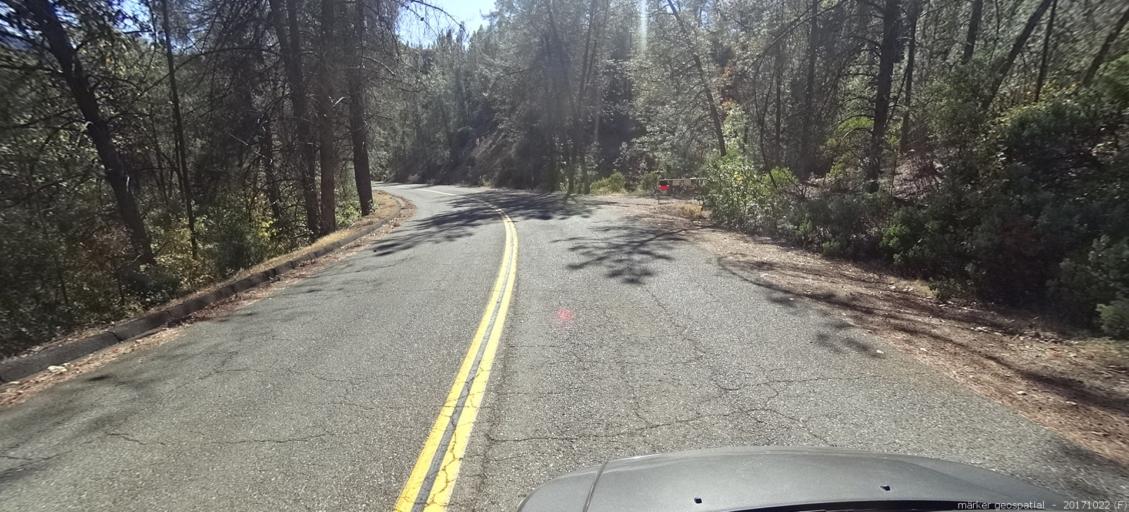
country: US
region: California
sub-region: Shasta County
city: Central Valley (historical)
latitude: 40.9196
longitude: -122.4024
